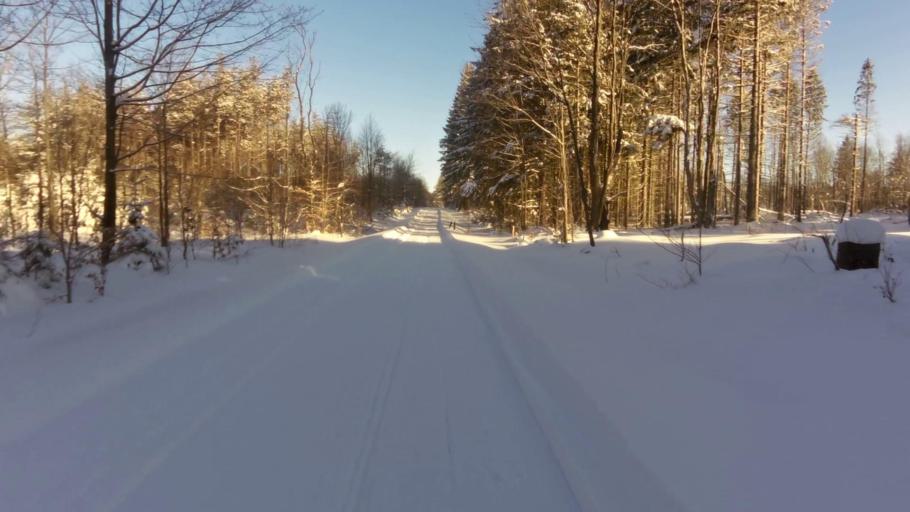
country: US
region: New York
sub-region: Chautauqua County
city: Falconer
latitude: 42.2427
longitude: -79.2131
